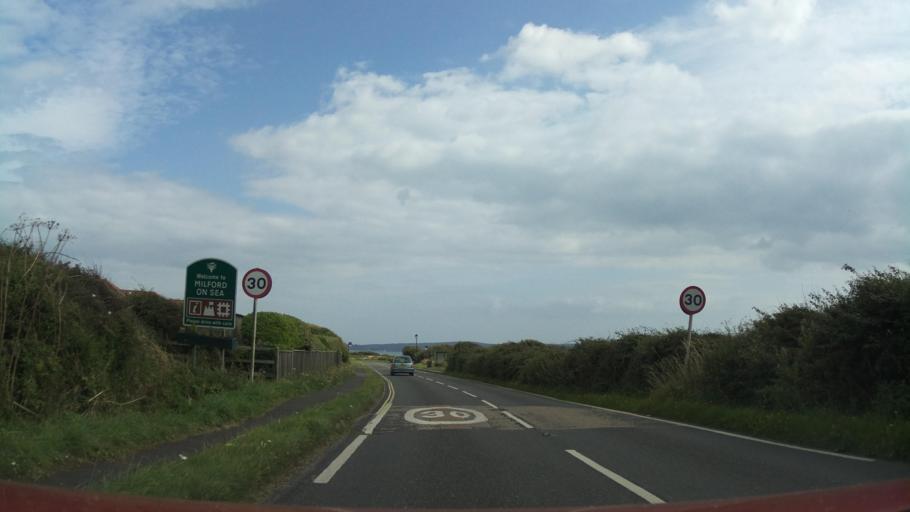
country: GB
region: England
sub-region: Hampshire
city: Milford on Sea
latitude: 50.7282
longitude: -1.6150
